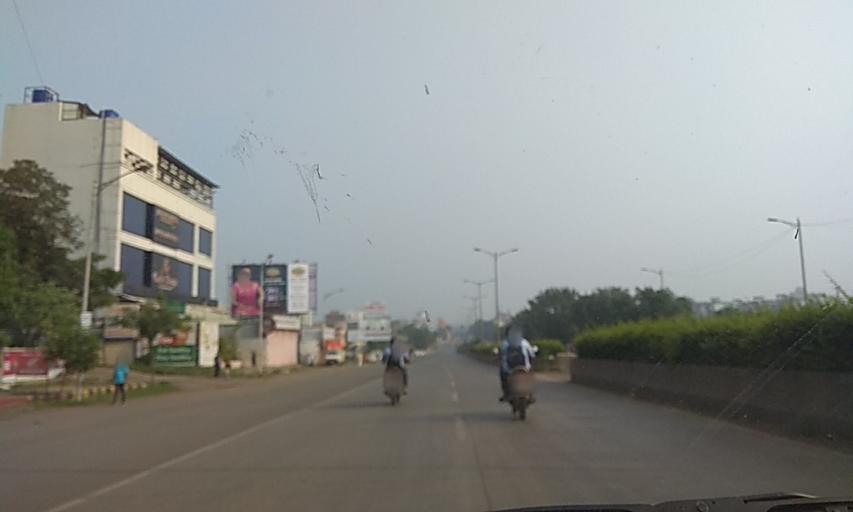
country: IN
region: Maharashtra
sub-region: Pune Division
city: Lohogaon
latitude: 18.5539
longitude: 73.9375
